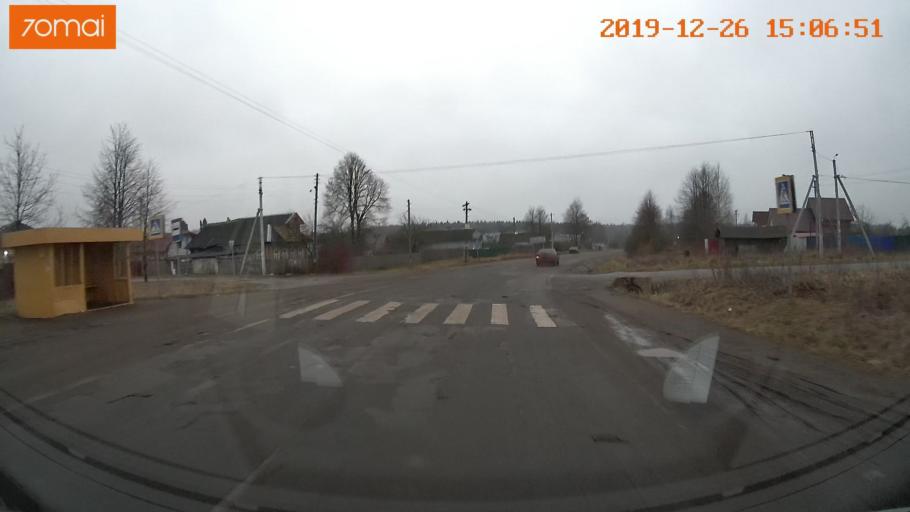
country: RU
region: Jaroslavl
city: Rybinsk
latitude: 58.1745
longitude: 38.8432
